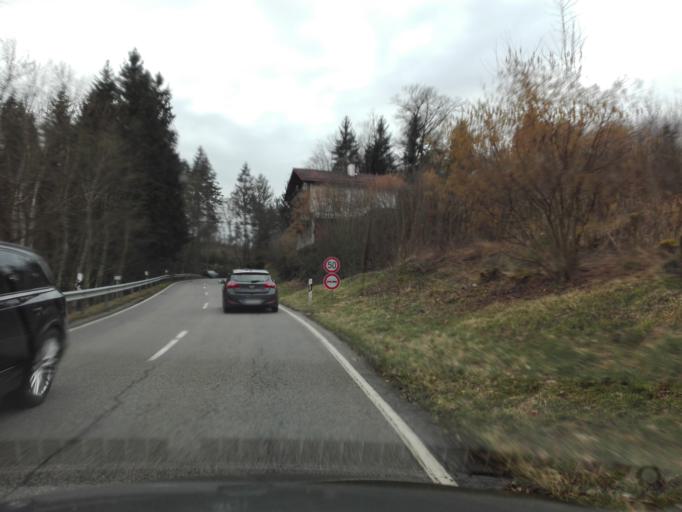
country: DE
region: Bavaria
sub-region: Lower Bavaria
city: Thyrnau
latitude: 48.5938
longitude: 13.5729
